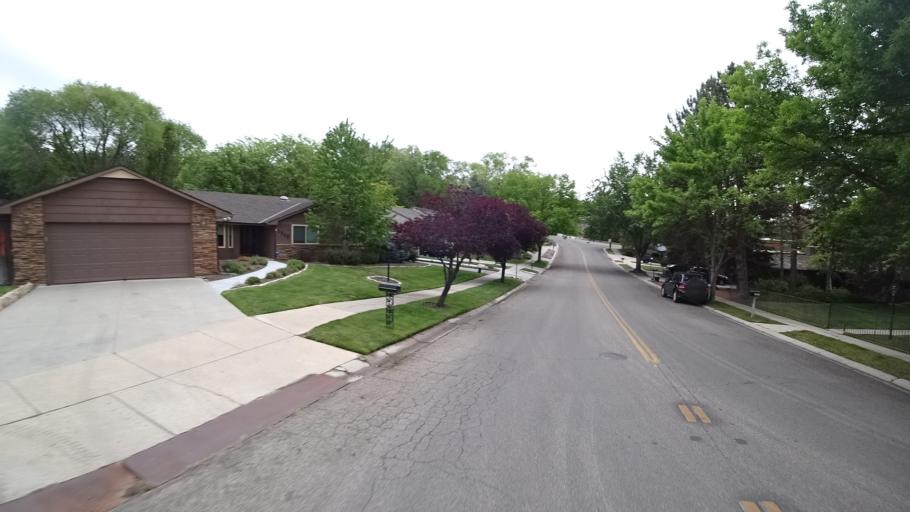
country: US
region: Idaho
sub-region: Ada County
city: Boise
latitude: 43.6125
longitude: -116.1762
